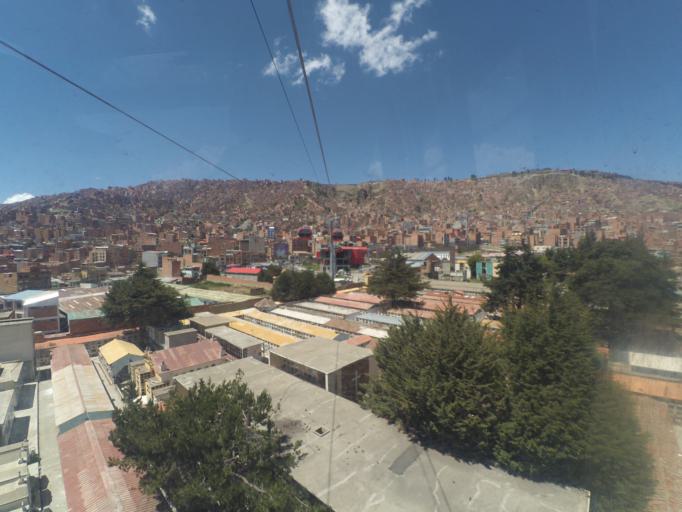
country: BO
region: La Paz
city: La Paz
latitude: -16.4968
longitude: -68.1512
